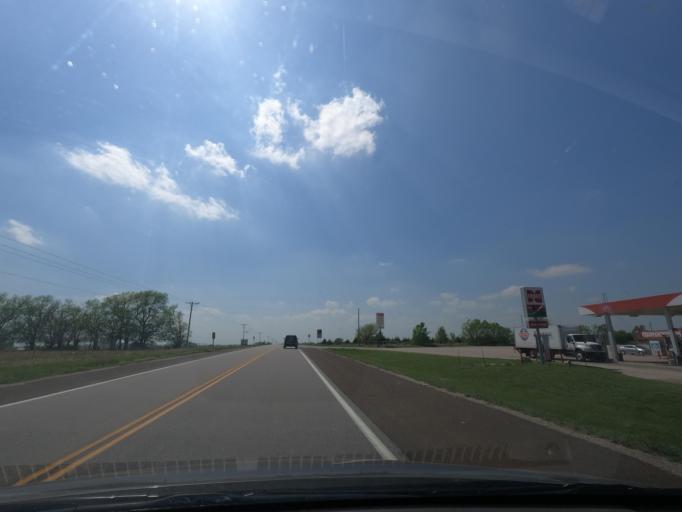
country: US
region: Kansas
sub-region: Butler County
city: El Dorado
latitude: 37.6791
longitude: -96.8160
